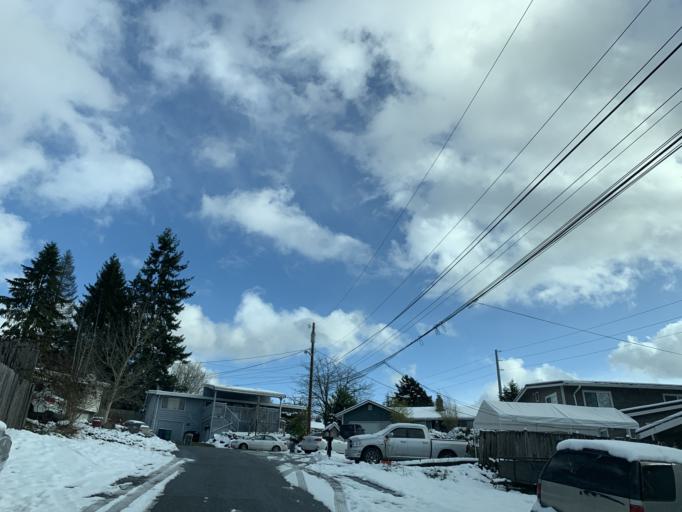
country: US
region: Washington
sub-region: Snohomish County
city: Martha Lake
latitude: 47.8506
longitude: -122.2629
